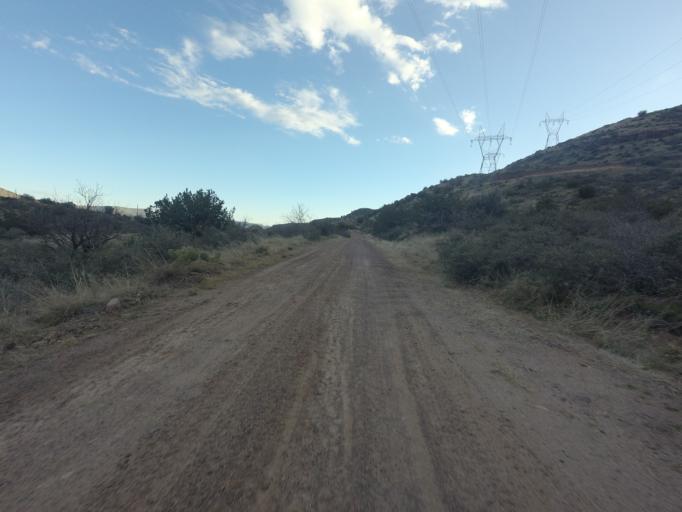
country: US
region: Arizona
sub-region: Gila County
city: Pine
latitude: 34.3648
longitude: -111.6756
